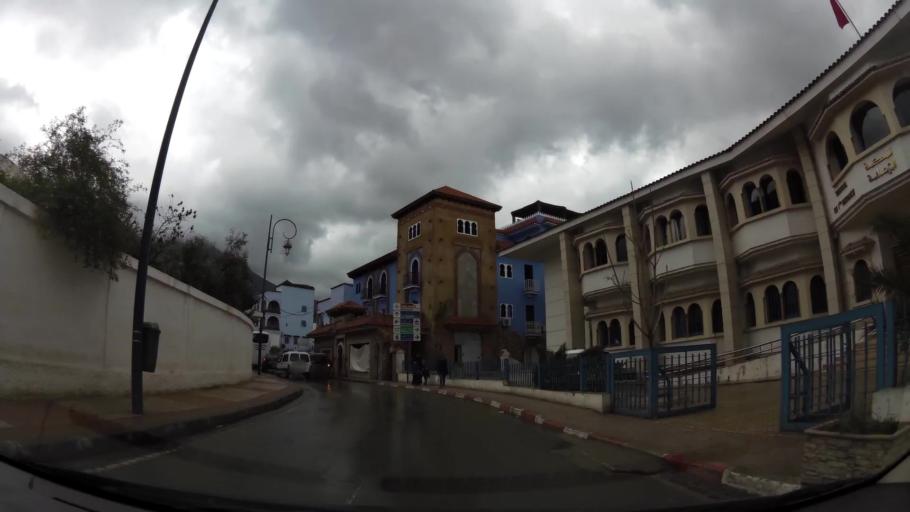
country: MA
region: Tanger-Tetouan
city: Chefchaouene
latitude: 35.1682
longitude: -5.2694
